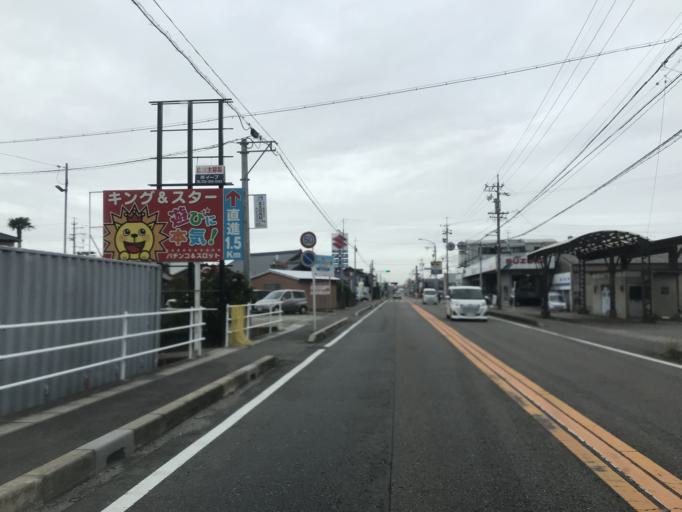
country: JP
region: Aichi
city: Nagoya-shi
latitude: 35.2130
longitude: 136.8502
